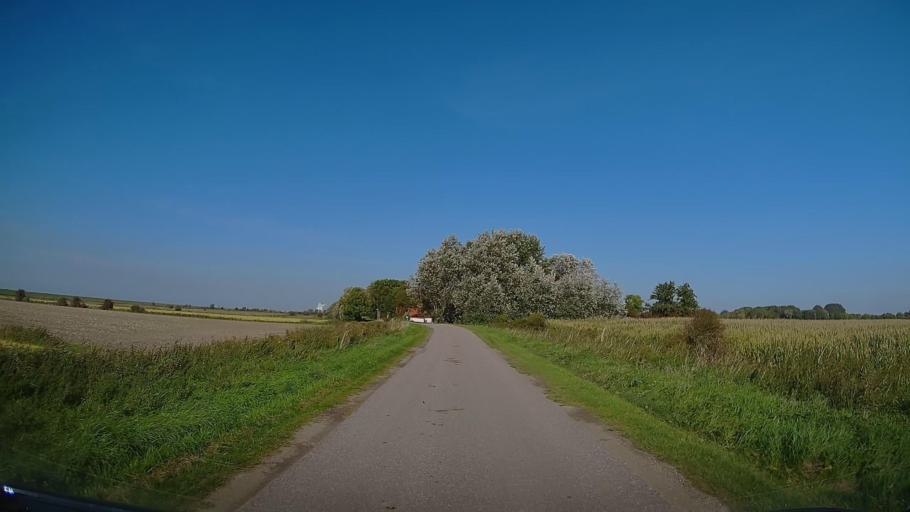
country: DE
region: Lower Saxony
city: Misselwarden
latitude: 53.6976
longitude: 8.4949
